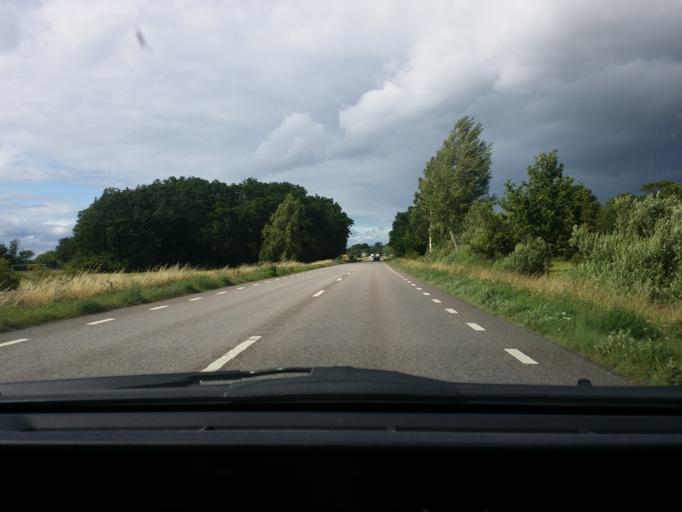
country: SE
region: Kalmar
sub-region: Borgholms Kommun
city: Borgholm
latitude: 56.8998
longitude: 16.7330
